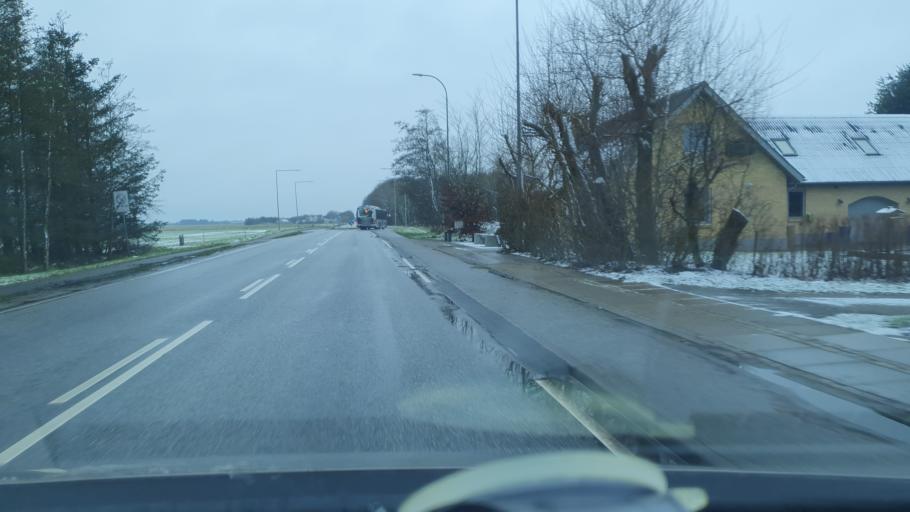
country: DK
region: North Denmark
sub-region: Jammerbugt Kommune
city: Kas
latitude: 57.1210
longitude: 9.6198
